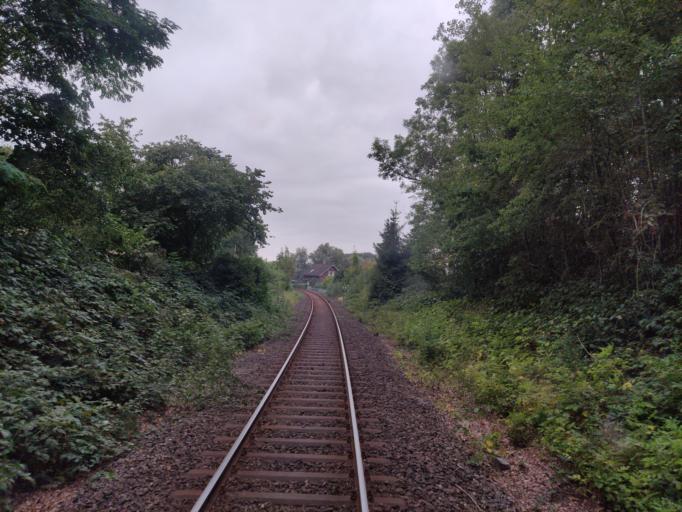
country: DE
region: Lower Saxony
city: Stade
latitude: 53.5903
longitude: 9.4907
